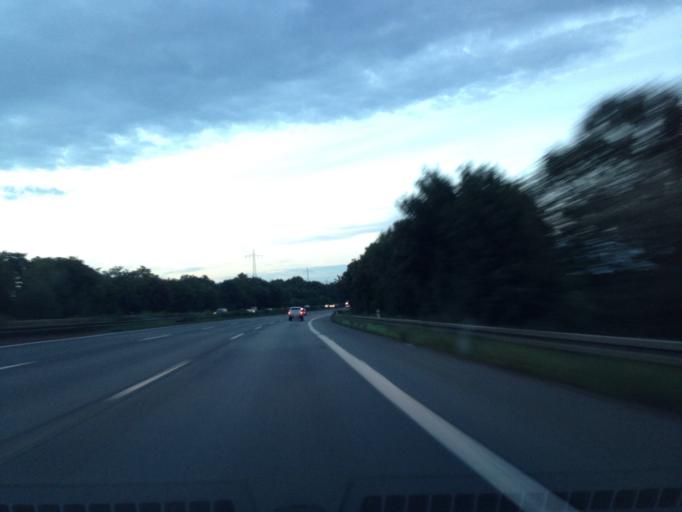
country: DE
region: North Rhine-Westphalia
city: Meiderich
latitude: 51.4521
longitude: 6.7993
